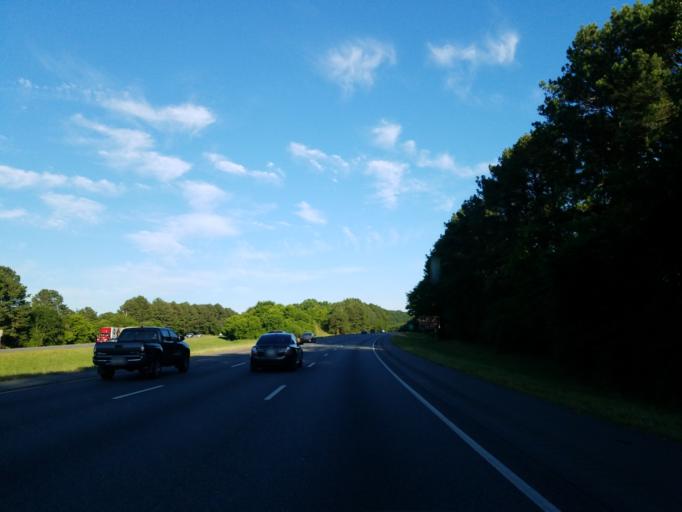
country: US
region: Georgia
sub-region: Bartow County
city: Cartersville
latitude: 34.2549
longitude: -84.7910
